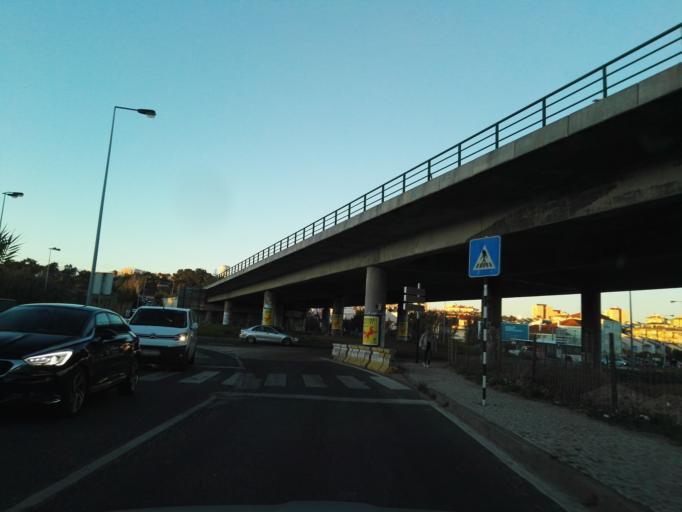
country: PT
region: Setubal
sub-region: Seixal
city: Corroios
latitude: 38.6414
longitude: -9.1488
